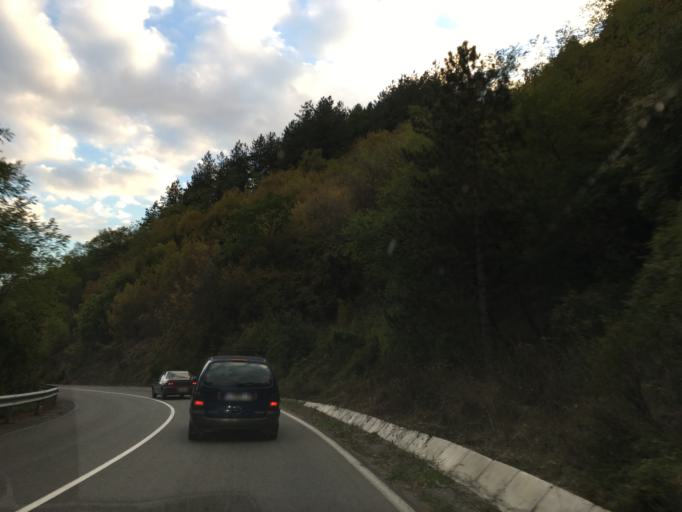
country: BG
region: Sofiya
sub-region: Obshtina Svoge
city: Svoge
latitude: 42.8784
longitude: 23.3754
